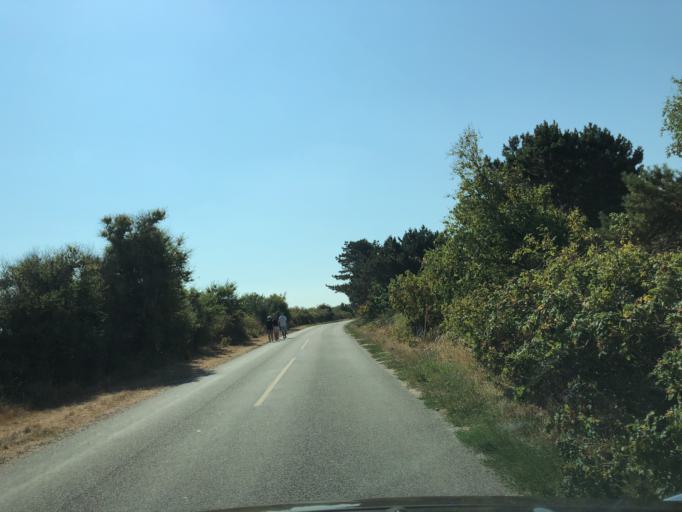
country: DK
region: Zealand
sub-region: Odsherred Kommune
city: Asnaes
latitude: 55.9919
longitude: 11.2944
